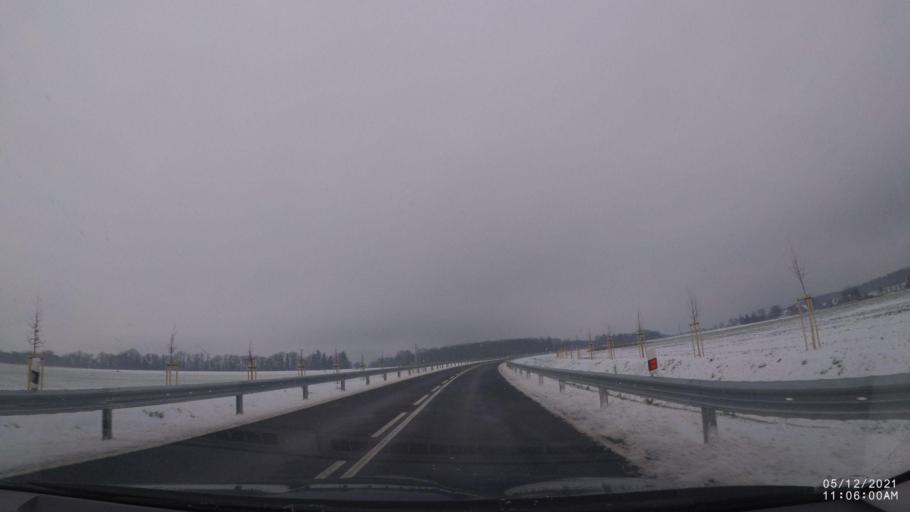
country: CZ
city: Solnice
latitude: 50.1797
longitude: 16.2188
